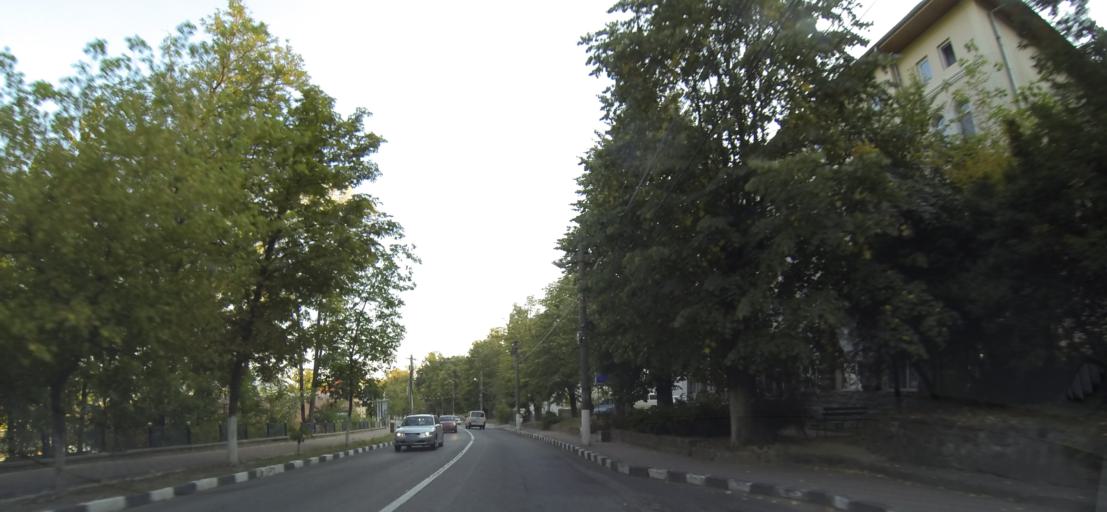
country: RO
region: Valcea
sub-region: Oras Calimanesti
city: Jiblea Veche
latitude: 45.2511
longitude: 24.3364
